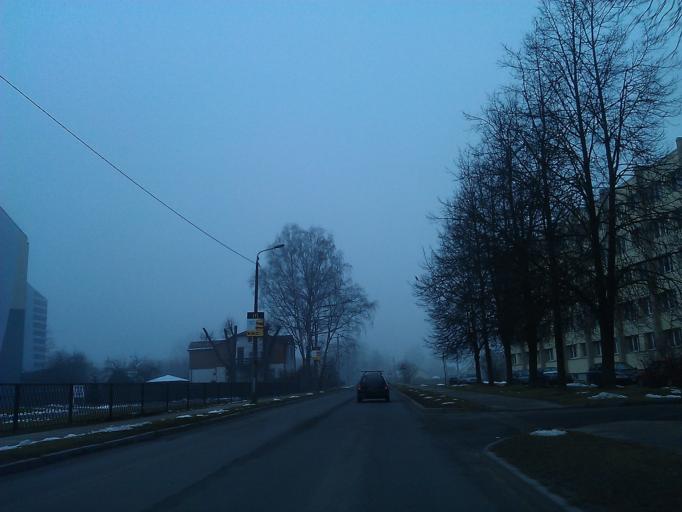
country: LV
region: Marupe
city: Marupe
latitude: 56.9113
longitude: 24.0809
